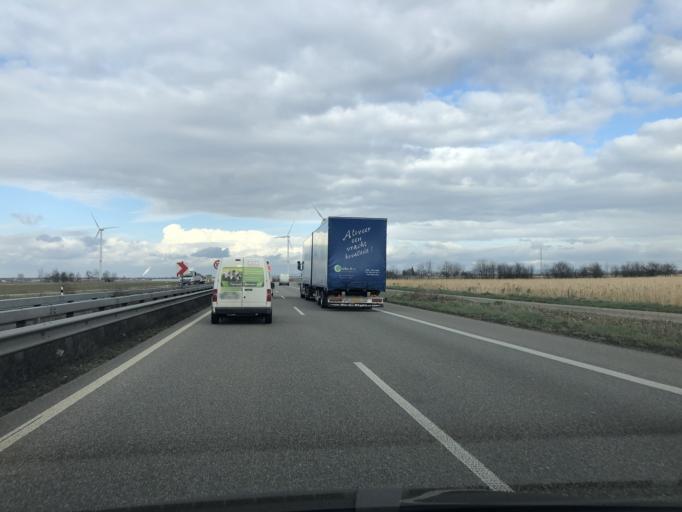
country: DE
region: Rheinland-Pfalz
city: Harthausen
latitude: 49.2877
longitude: 8.3700
